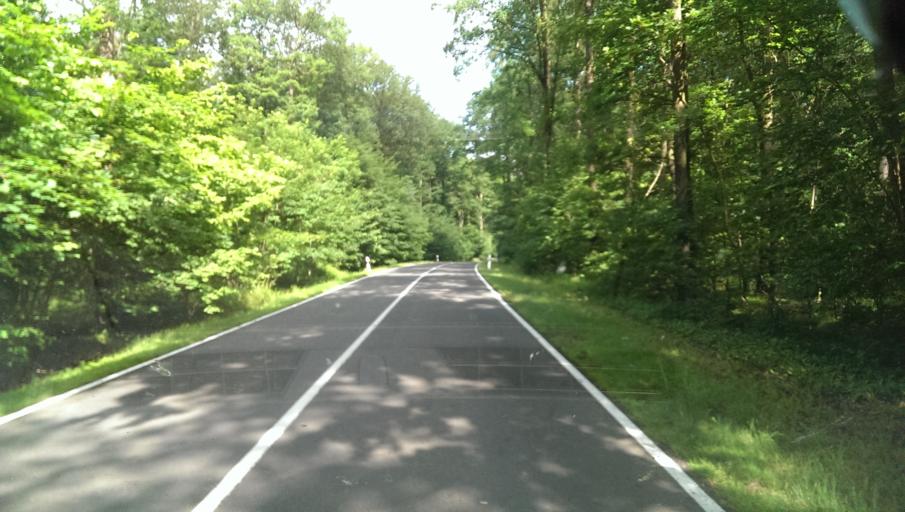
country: DE
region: Saxony-Anhalt
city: Eckartsberga
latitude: 51.1458
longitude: 11.5637
